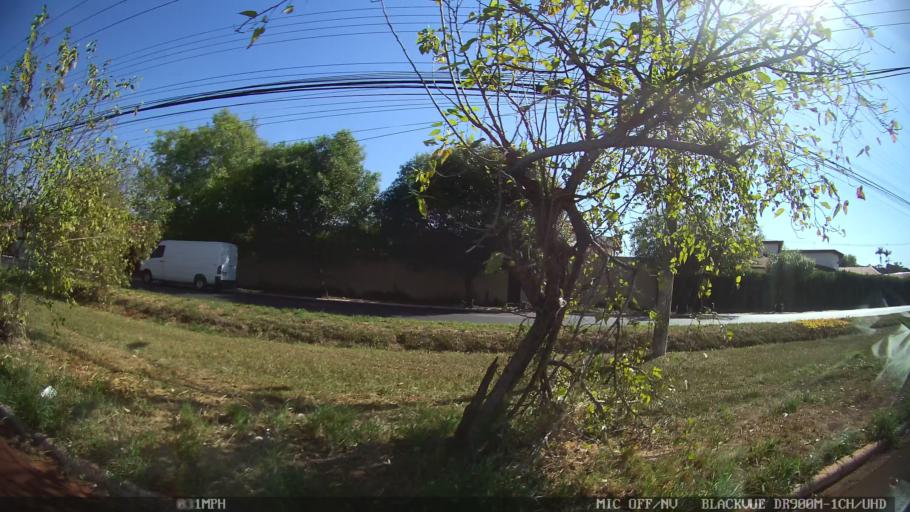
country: BR
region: Sao Paulo
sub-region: Ribeirao Preto
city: Ribeirao Preto
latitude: -21.1897
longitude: -47.7609
